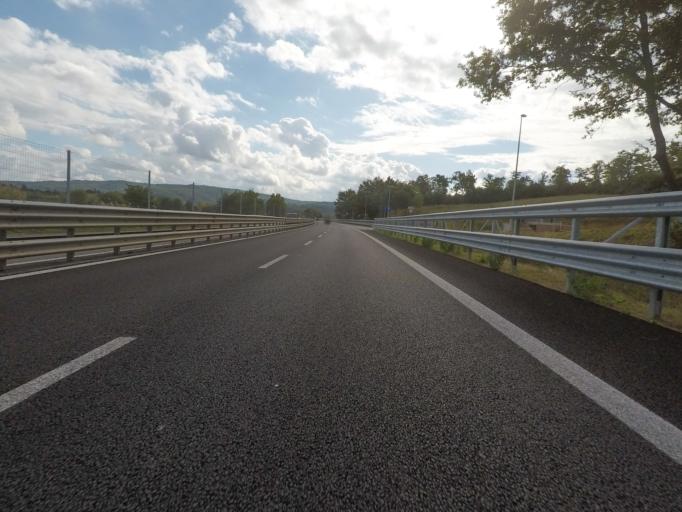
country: IT
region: Tuscany
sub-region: Provincia di Siena
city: Serre di Rapolano
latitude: 43.2541
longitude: 11.6360
